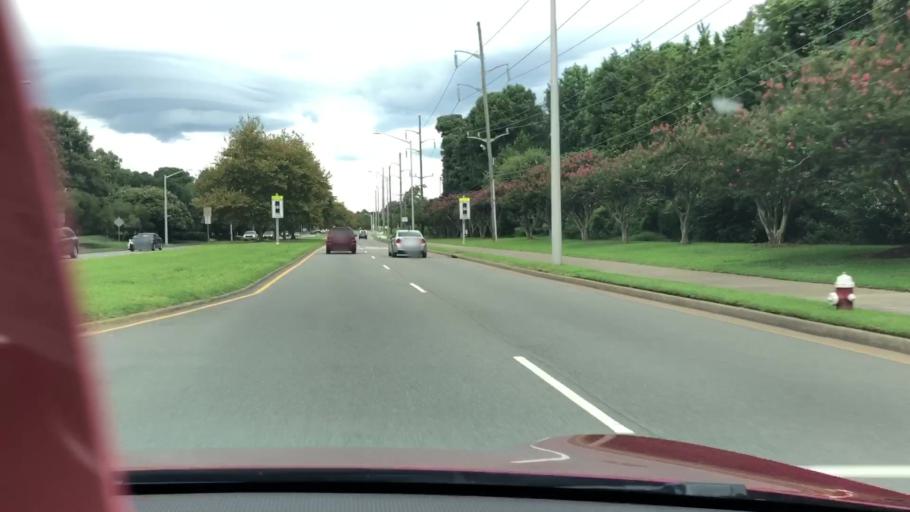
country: US
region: Virginia
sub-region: City of Virginia Beach
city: Virginia Beach
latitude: 36.8940
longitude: -76.0584
